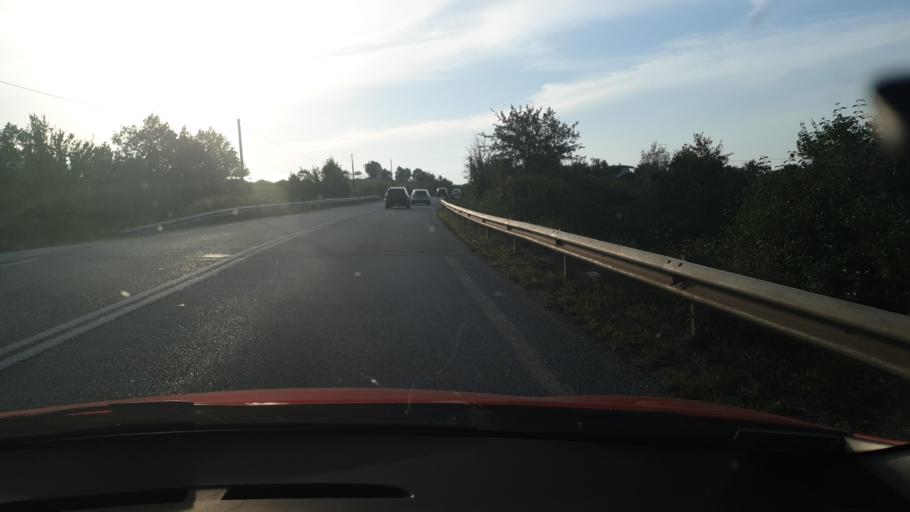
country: GR
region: Central Macedonia
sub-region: Nomos Chalkidikis
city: Galatista
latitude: 40.4613
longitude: 23.3789
